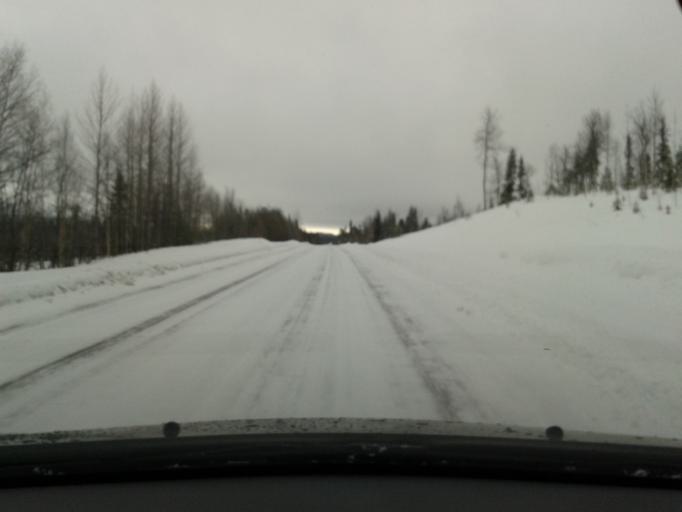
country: SE
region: Vaesterbotten
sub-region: Vilhelmina Kommun
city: Sjoberg
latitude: 64.8790
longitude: 15.8714
